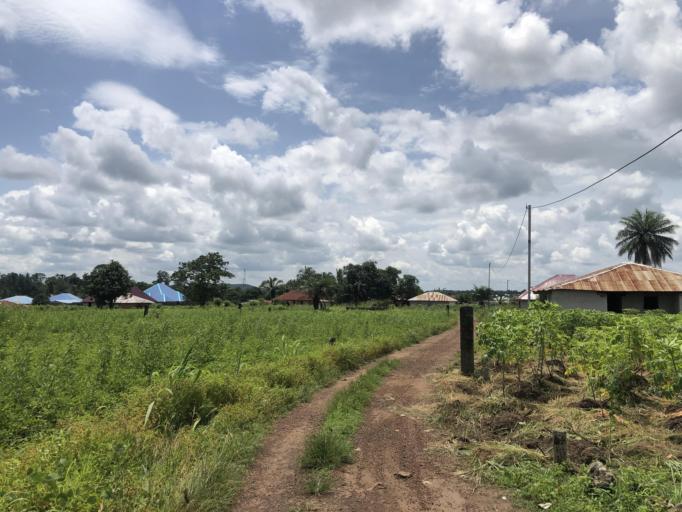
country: SL
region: Northern Province
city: Magburaka
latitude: 8.7053
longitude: -11.9240
